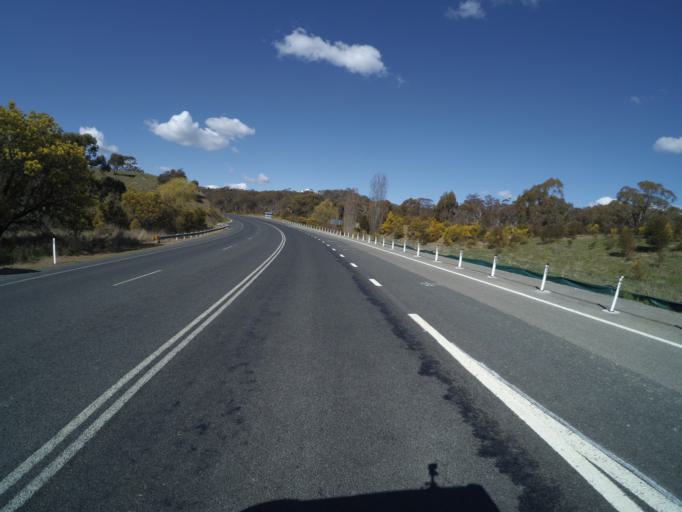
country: AU
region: New South Wales
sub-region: Queanbeyan
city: Queanbeyan
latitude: -35.3462
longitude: 149.2726
